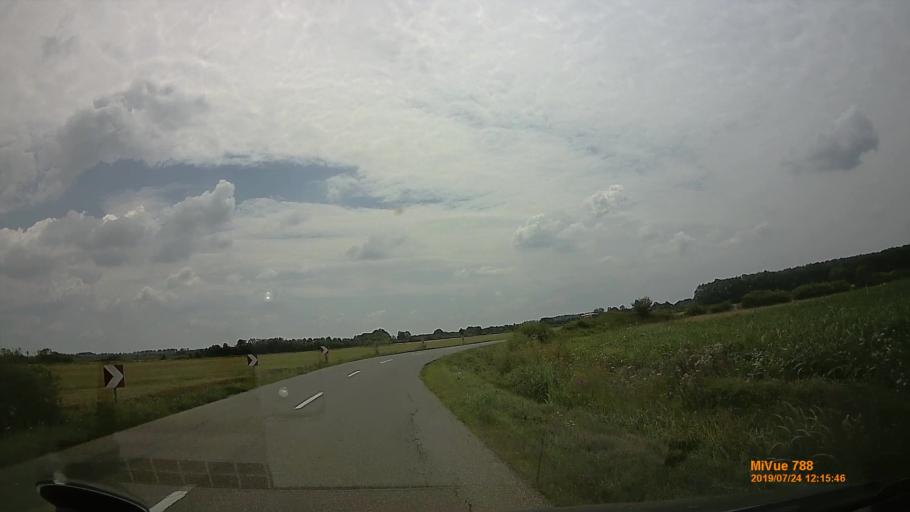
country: HU
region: Szabolcs-Szatmar-Bereg
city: Vasarosnameny
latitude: 48.1799
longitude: 22.3466
